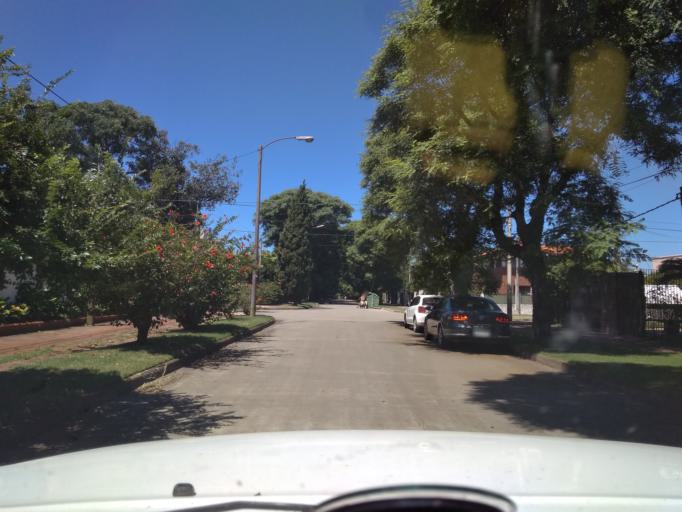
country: UY
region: Canelones
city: Paso de Carrasco
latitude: -34.8923
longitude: -56.0652
